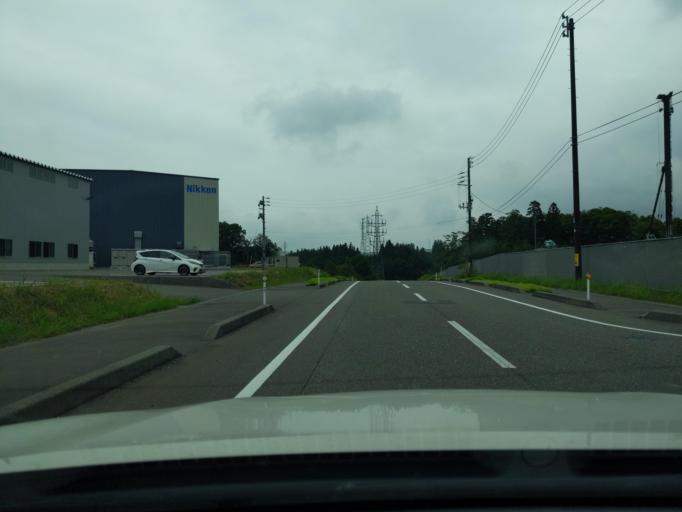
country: JP
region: Niigata
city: Kashiwazaki
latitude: 37.3400
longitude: 138.5910
